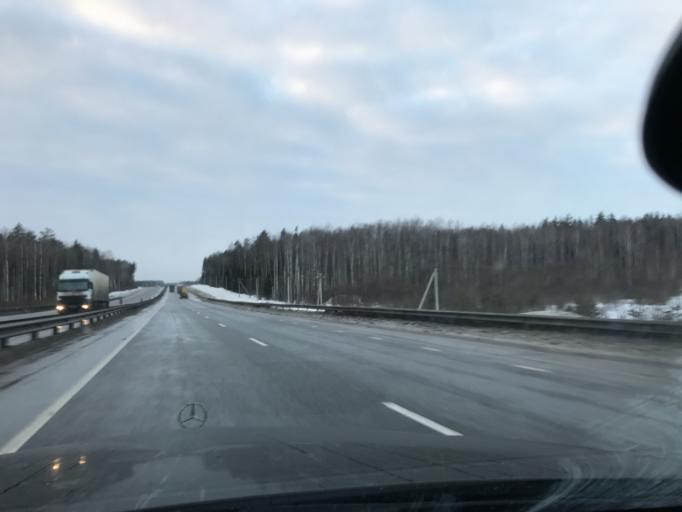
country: RU
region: Vladimir
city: Orgtrud
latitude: 56.1034
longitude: 40.6811
